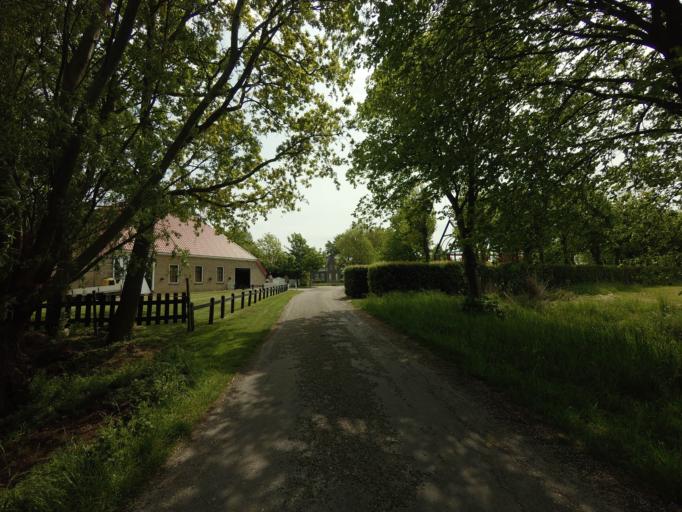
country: NL
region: Friesland
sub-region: Sudwest Fryslan
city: Bolsward
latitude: 53.0997
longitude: 5.4821
